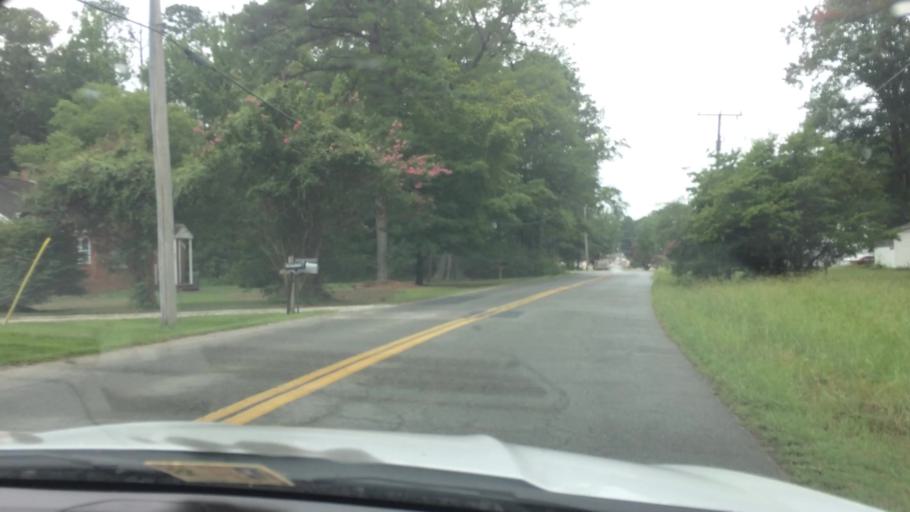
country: US
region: Virginia
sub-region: King William County
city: West Point
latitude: 37.5500
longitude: -76.8036
